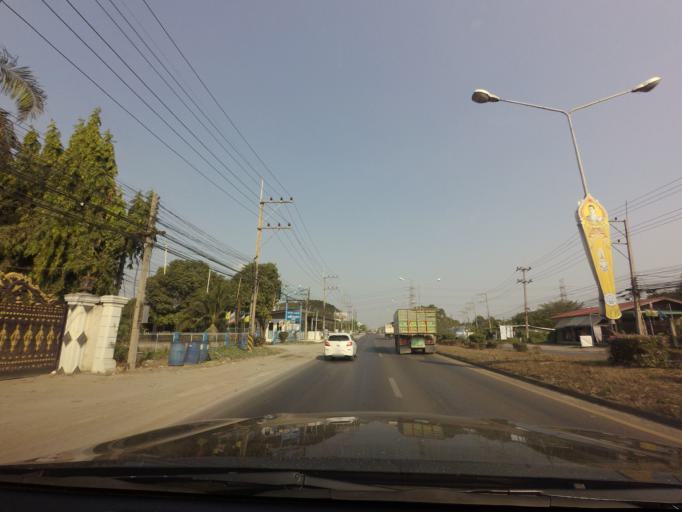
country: TH
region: Ratchaburi
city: Ban Pong
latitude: 13.8480
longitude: 99.8555
